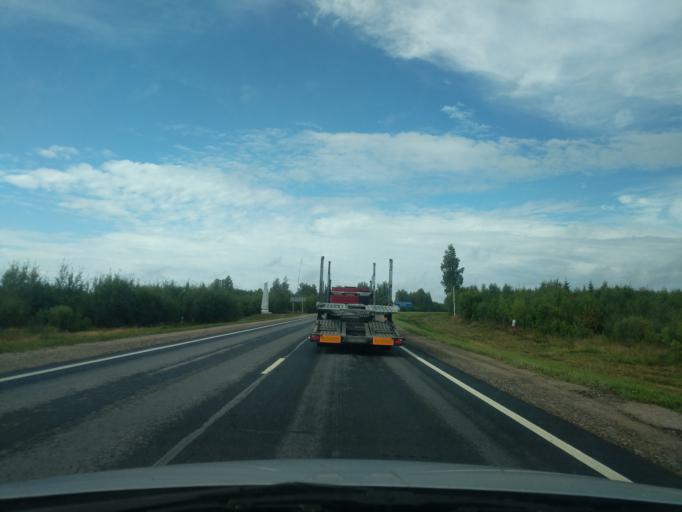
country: RU
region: Kostroma
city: Sudislavl'
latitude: 57.8224
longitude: 41.9018
